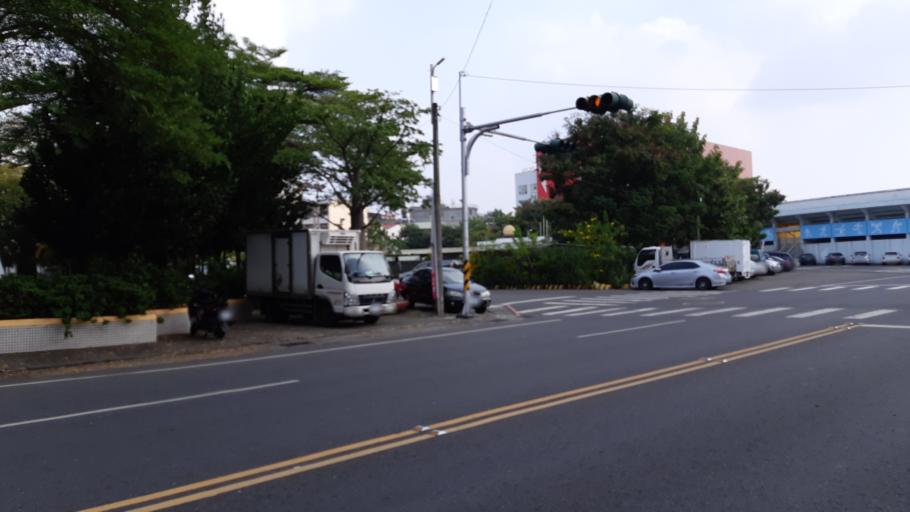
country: TW
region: Taiwan
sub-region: Chiayi
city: Jiayi Shi
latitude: 23.4732
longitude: 120.4617
